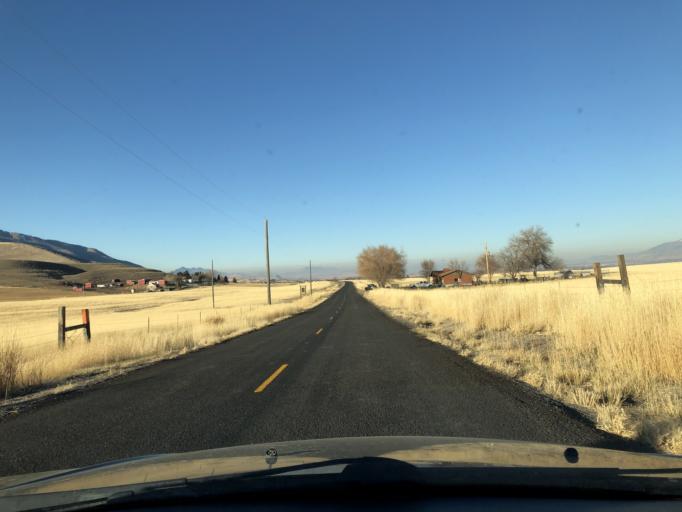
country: US
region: Utah
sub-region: Cache County
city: Wellsville
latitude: 41.5872
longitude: -111.9261
